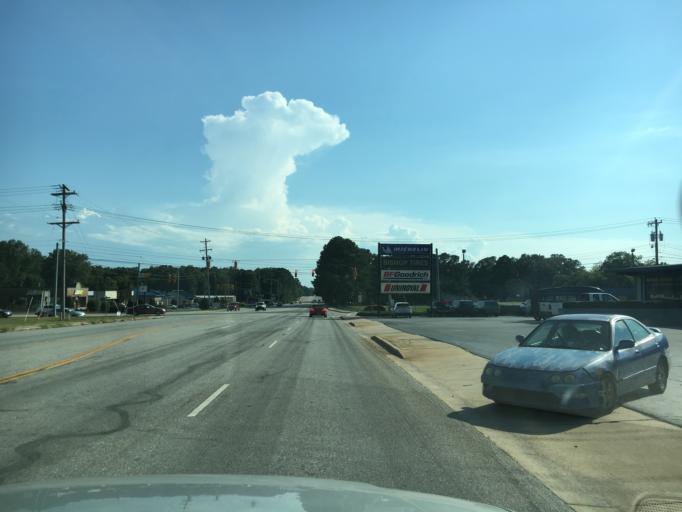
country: US
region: South Carolina
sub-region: Laurens County
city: Clinton
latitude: 34.4545
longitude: -81.8812
